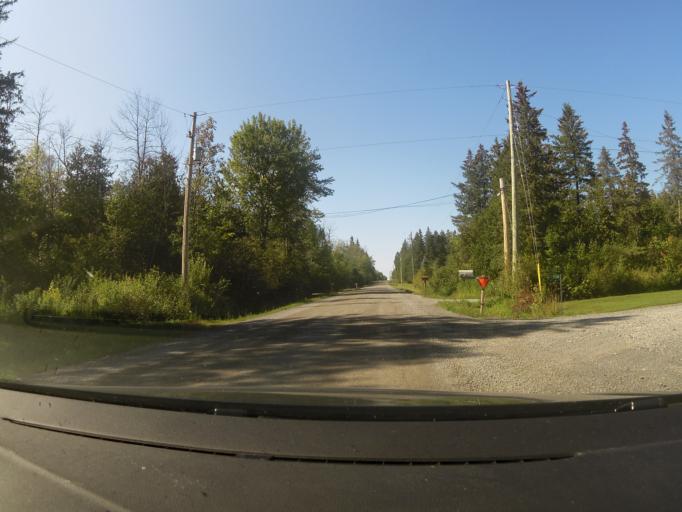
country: CA
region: Ontario
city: Carleton Place
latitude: 45.3174
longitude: -76.0724
